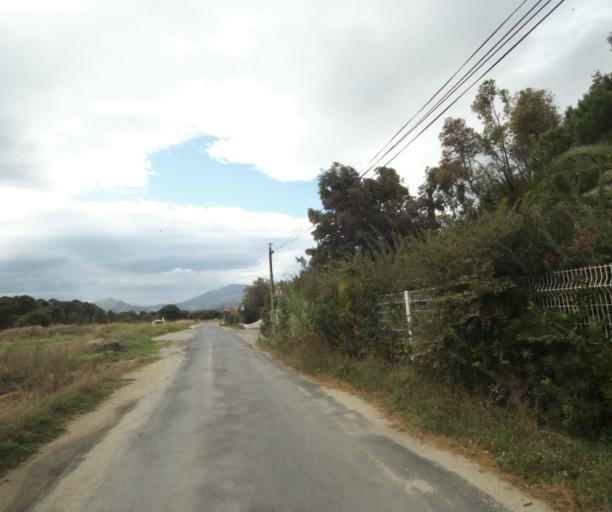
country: FR
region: Languedoc-Roussillon
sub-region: Departement des Pyrenees-Orientales
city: Argelers
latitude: 42.5728
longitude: 3.0412
